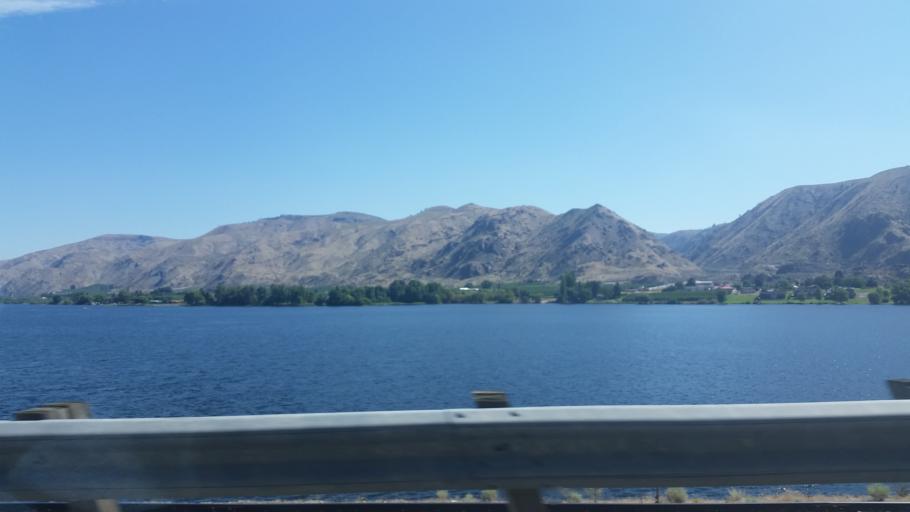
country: US
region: Washington
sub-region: Chelan County
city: Entiat
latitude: 47.6242
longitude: -120.2402
